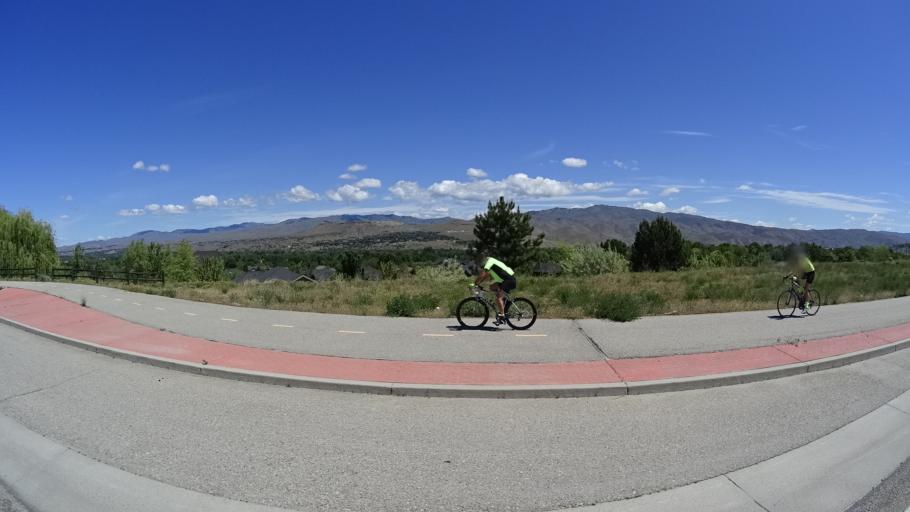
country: US
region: Idaho
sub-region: Ada County
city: Boise
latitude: 43.5624
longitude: -116.1715
